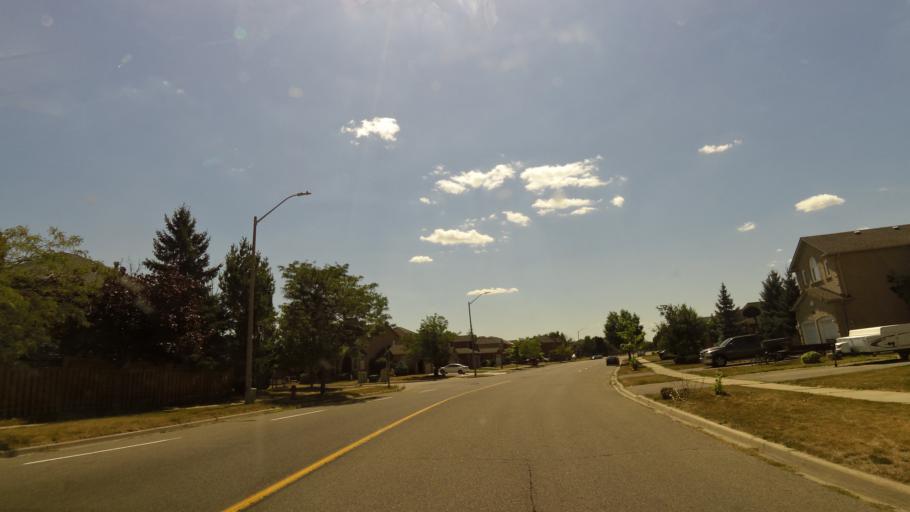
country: CA
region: Ontario
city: Brampton
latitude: 43.6406
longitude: -79.8725
